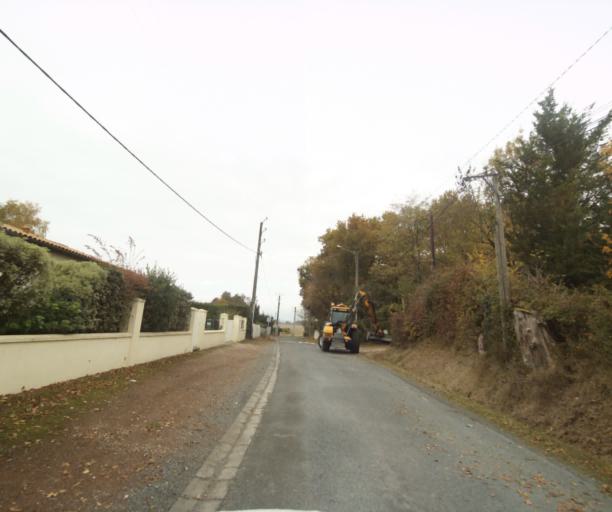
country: FR
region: Poitou-Charentes
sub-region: Departement de la Charente-Maritime
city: Saintes
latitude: 45.7371
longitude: -0.6724
